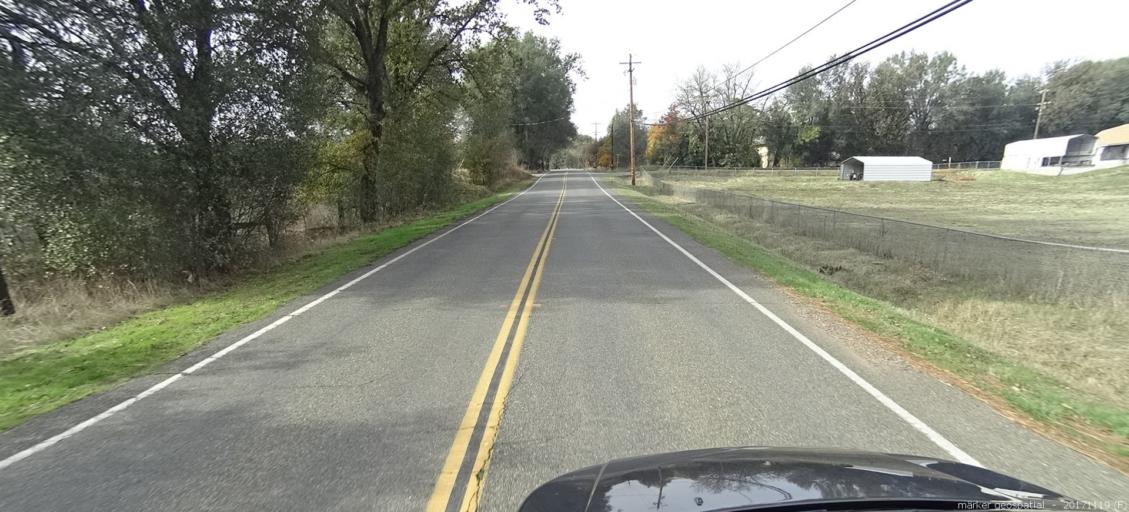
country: US
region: California
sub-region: Shasta County
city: Anderson
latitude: 40.4984
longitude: -122.3165
